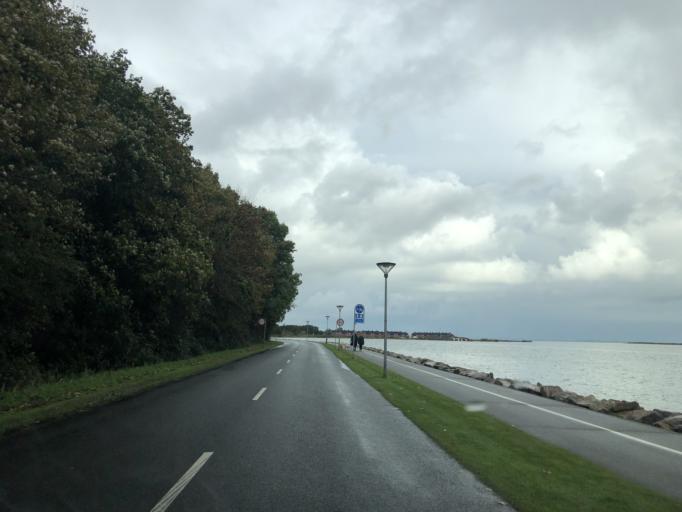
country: DK
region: Central Jutland
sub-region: Lemvig Kommune
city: Lemvig
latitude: 56.5582
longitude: 8.2954
